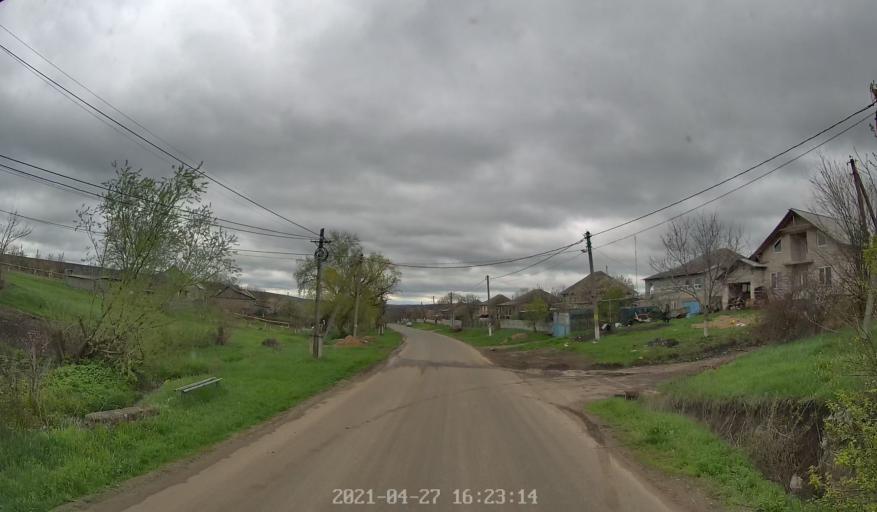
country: MD
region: Chisinau
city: Singera
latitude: 47.0001
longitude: 29.0169
